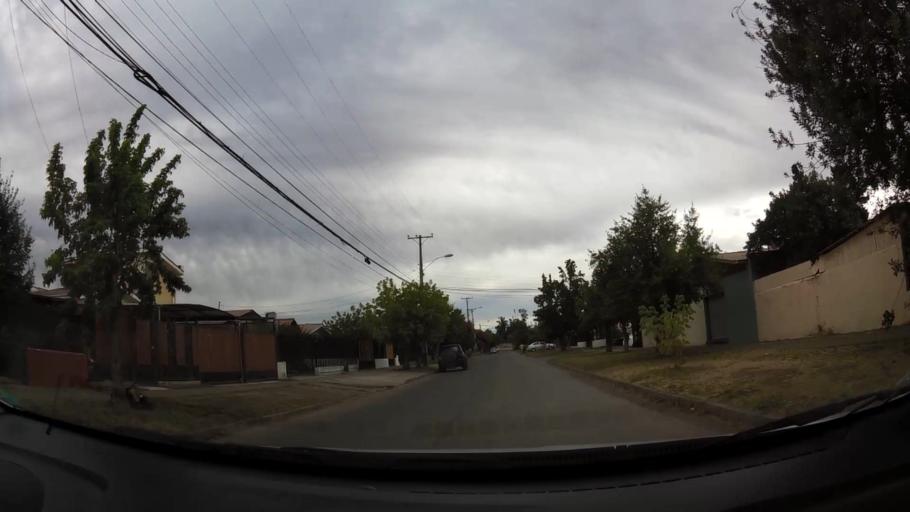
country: CL
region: O'Higgins
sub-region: Provincia de Cachapoal
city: Rancagua
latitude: -34.1513
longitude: -70.7460
